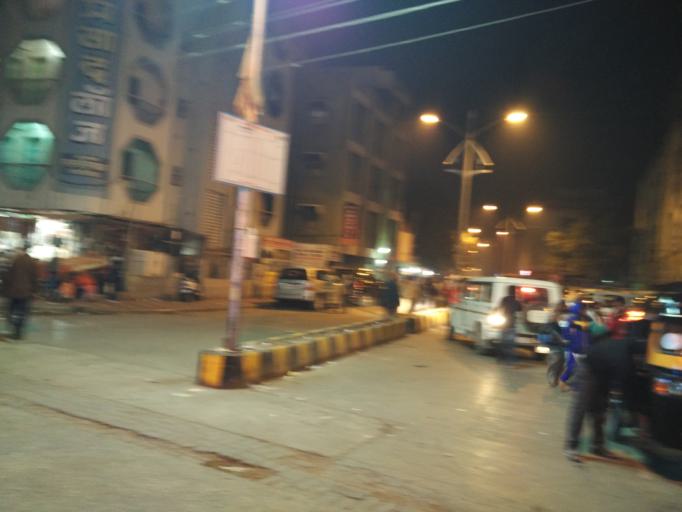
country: IN
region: Maharashtra
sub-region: Ahmadnagar
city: Shirdi
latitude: 19.7671
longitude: 74.4769
